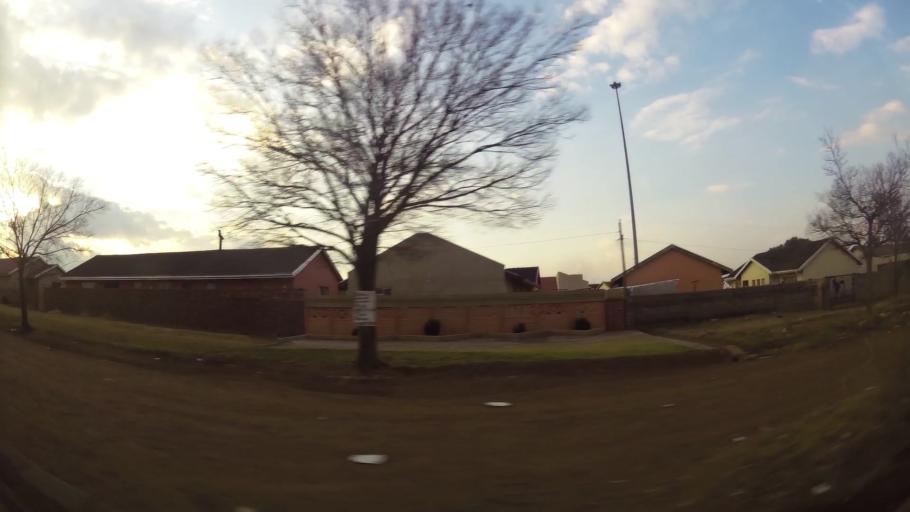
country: ZA
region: Gauteng
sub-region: City of Johannesburg Metropolitan Municipality
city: Orange Farm
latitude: -26.5930
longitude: 27.8487
